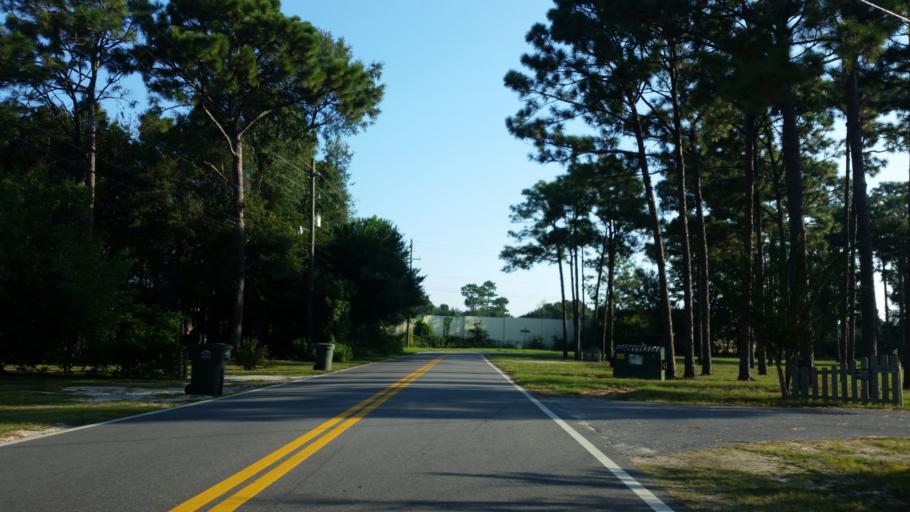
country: US
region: Florida
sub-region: Escambia County
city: Ferry Pass
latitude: 30.5010
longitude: -87.1755
